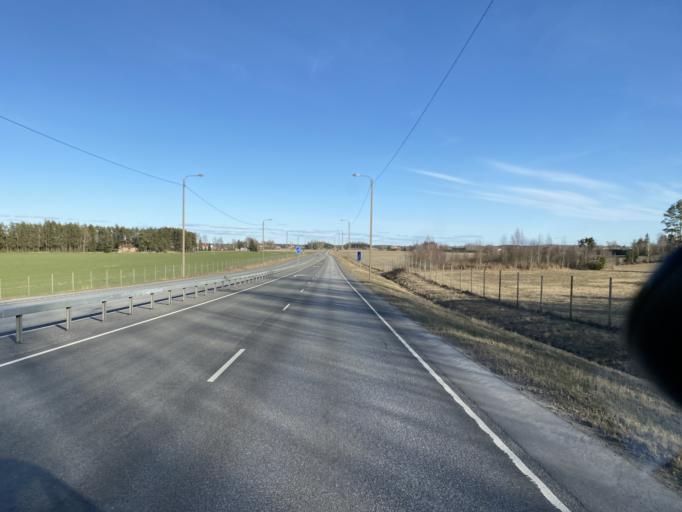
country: FI
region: Satakunta
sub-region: Pori
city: Huittinen
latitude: 61.1738
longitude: 22.6498
